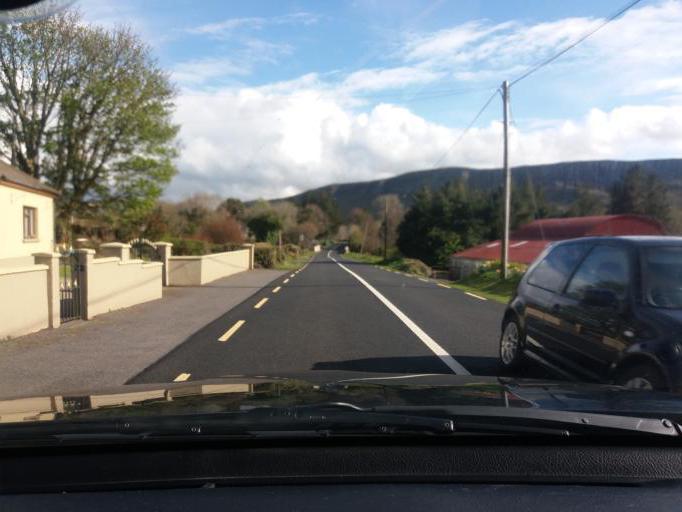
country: IE
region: Connaught
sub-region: County Leitrim
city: Kinlough
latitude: 54.3826
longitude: -8.2977
